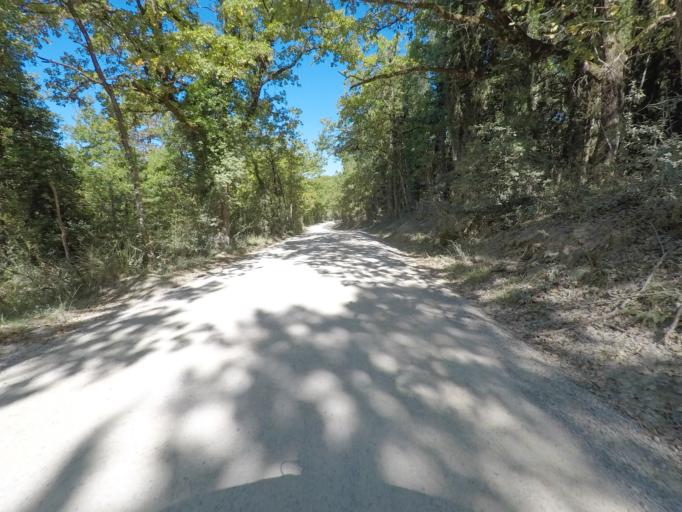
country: IT
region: Tuscany
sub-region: Provincia di Siena
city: Castellina in Chianti
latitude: 43.4367
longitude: 11.3113
